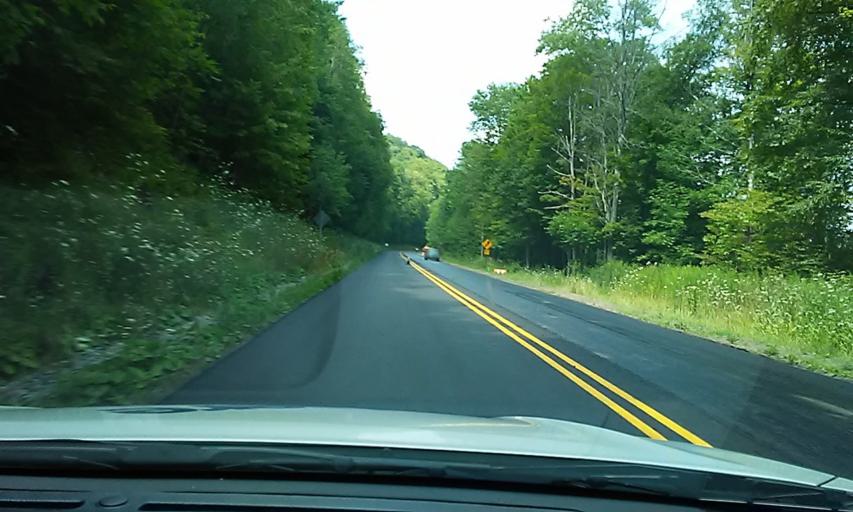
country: US
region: Pennsylvania
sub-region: Cameron County
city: Emporium
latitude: 41.6327
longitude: -78.1990
